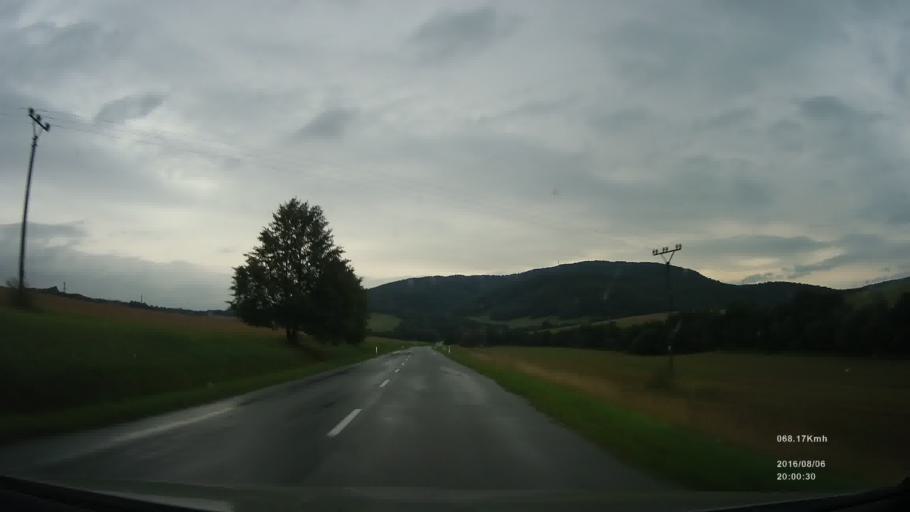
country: SK
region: Presovsky
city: Svidnik
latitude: 49.2519
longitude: 21.5818
